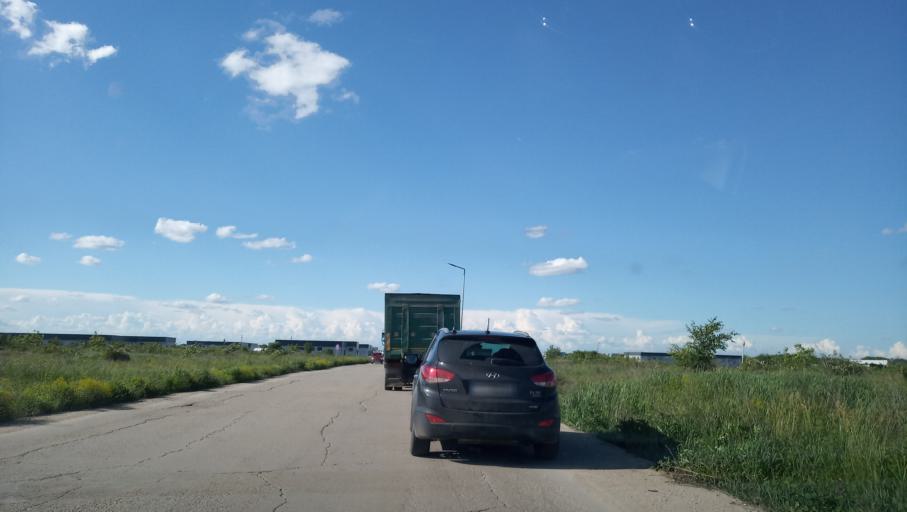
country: RO
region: Ilfov
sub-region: Comuna Dragomiresti-Vale
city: Dragomiresti-Deal
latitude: 44.4483
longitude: 25.9579
